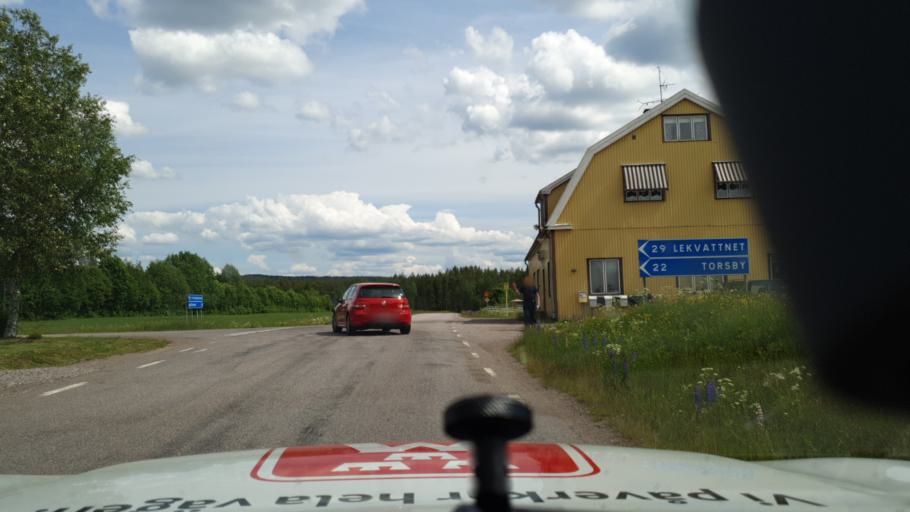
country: SE
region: Vaermland
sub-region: Torsby Kommun
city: Torsby
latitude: 59.9838
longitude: 12.8731
